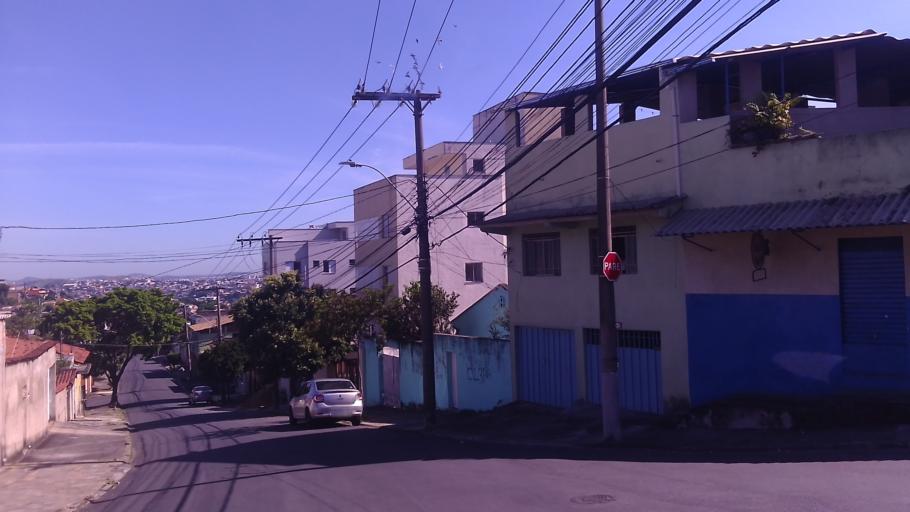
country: BR
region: Minas Gerais
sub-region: Contagem
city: Contagem
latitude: -19.9185
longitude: -44.0019
